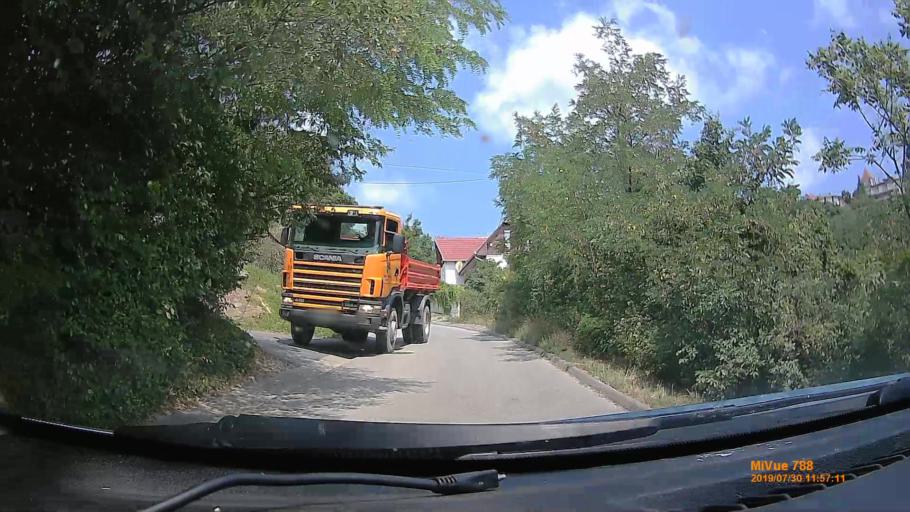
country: HU
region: Baranya
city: Pecs
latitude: 46.0863
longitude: 18.2179
